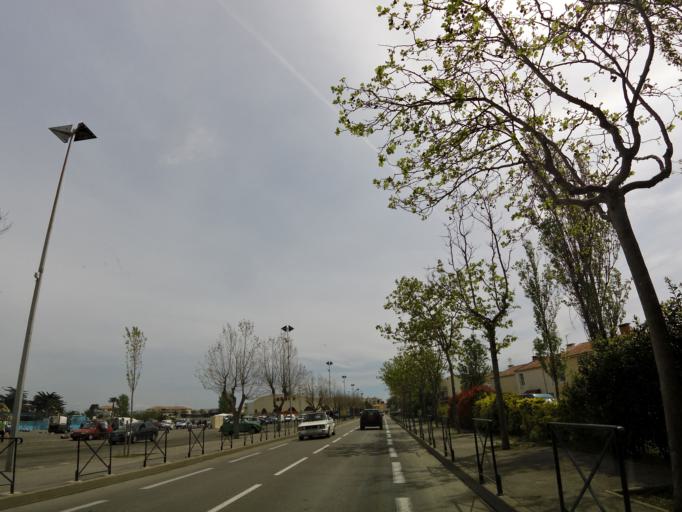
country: FR
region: Languedoc-Roussillon
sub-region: Departement de l'Herault
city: Palavas-les-Flots
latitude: 43.5314
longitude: 3.9276
